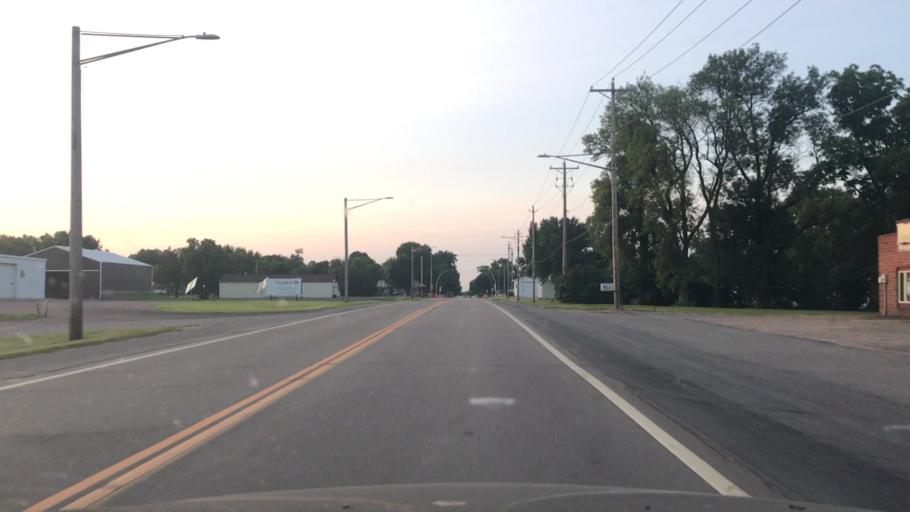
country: US
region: Minnesota
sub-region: Redwood County
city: Redwood Falls
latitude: 44.5304
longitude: -95.1194
